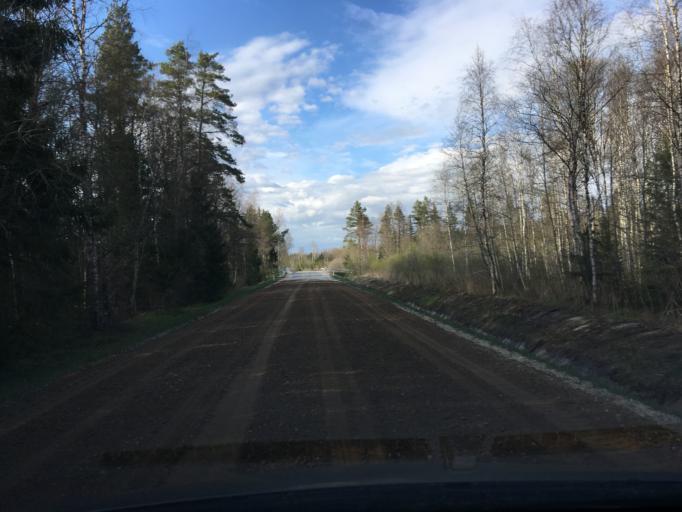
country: EE
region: Raplamaa
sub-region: Maerjamaa vald
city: Marjamaa
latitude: 58.9919
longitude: 24.3668
